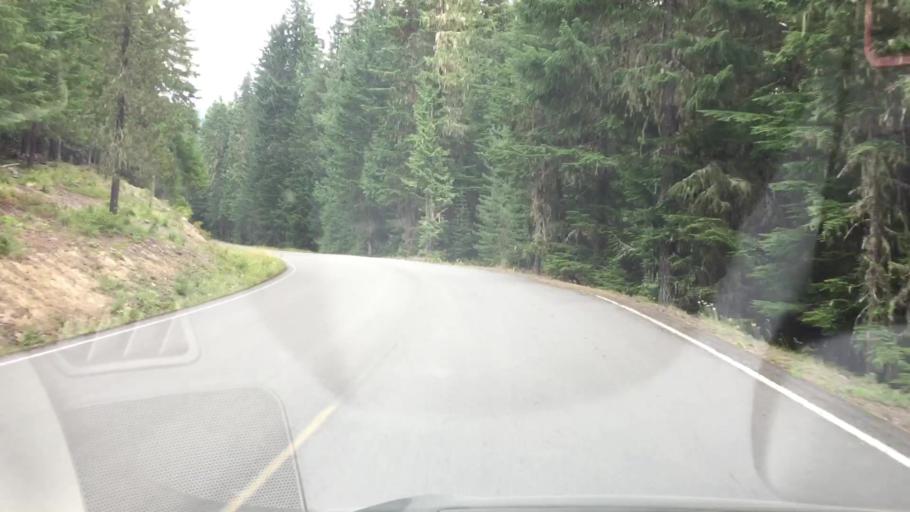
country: US
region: Washington
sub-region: Klickitat County
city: White Salmon
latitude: 46.2148
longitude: -121.6357
